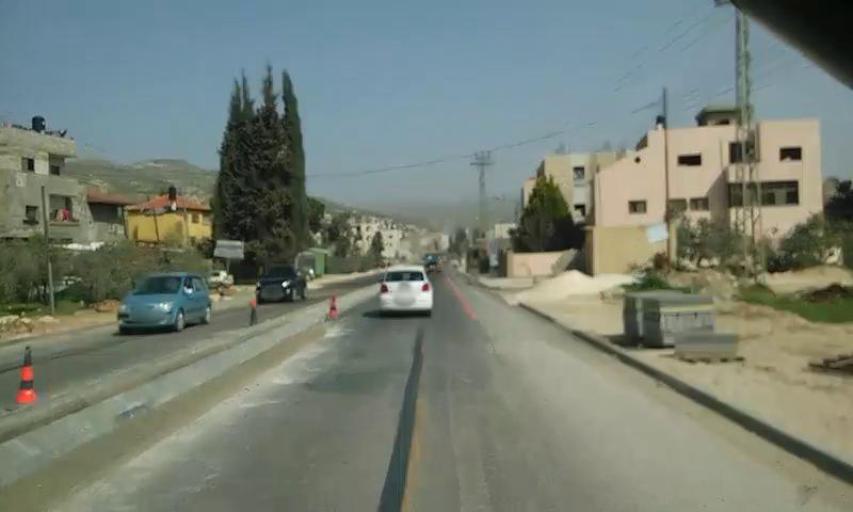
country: PS
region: West Bank
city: Huwwarah
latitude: 32.1400
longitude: 35.2580
